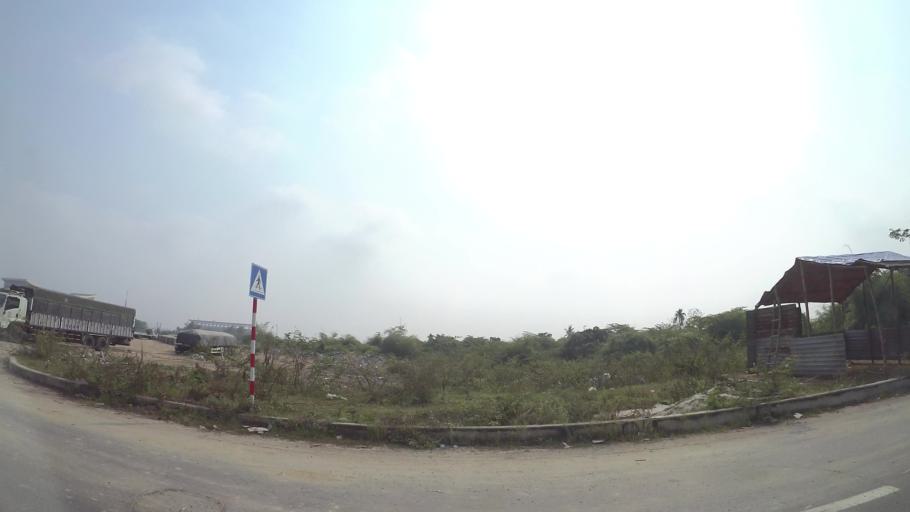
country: VN
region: Da Nang
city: Cam Le
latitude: 15.9946
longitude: 108.2163
